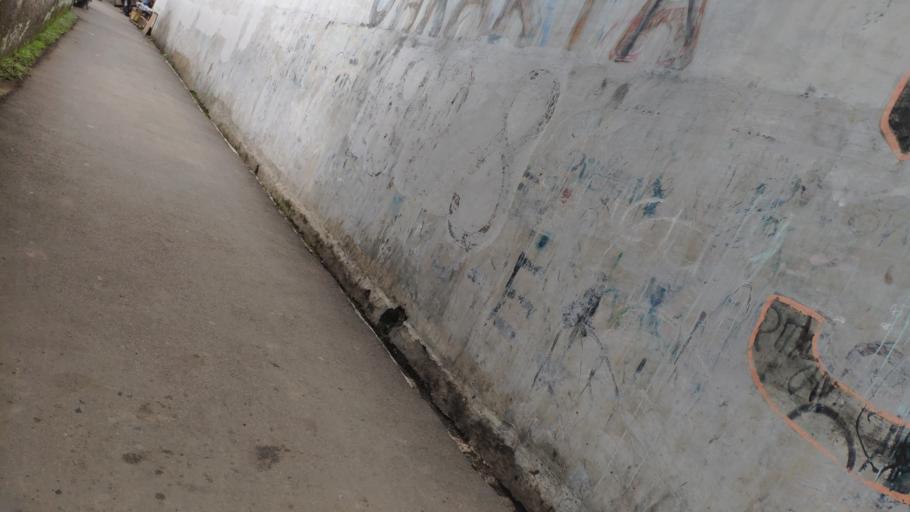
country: ID
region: West Java
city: Depok
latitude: -6.3503
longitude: 106.8010
